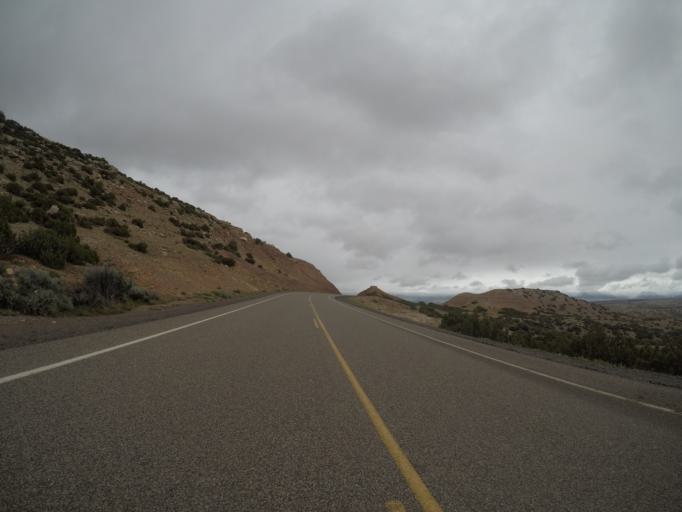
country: US
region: Wyoming
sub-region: Big Horn County
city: Lovell
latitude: 45.0347
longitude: -108.2595
